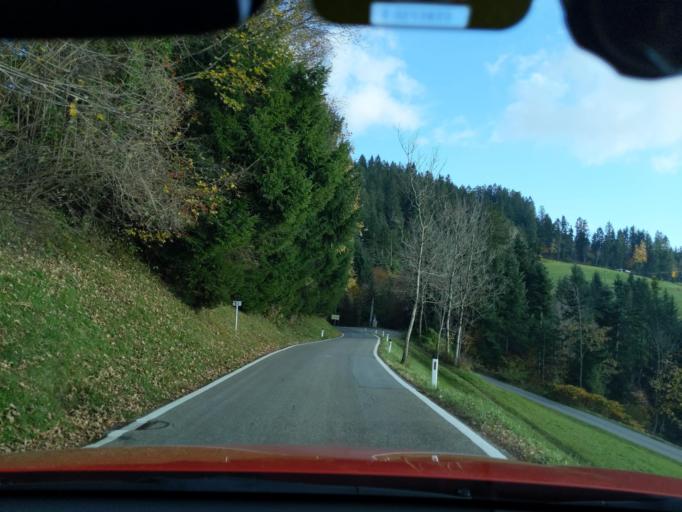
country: AT
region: Vorarlberg
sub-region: Politischer Bezirk Bregenz
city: Eichenberg
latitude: 47.5521
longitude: 9.7844
